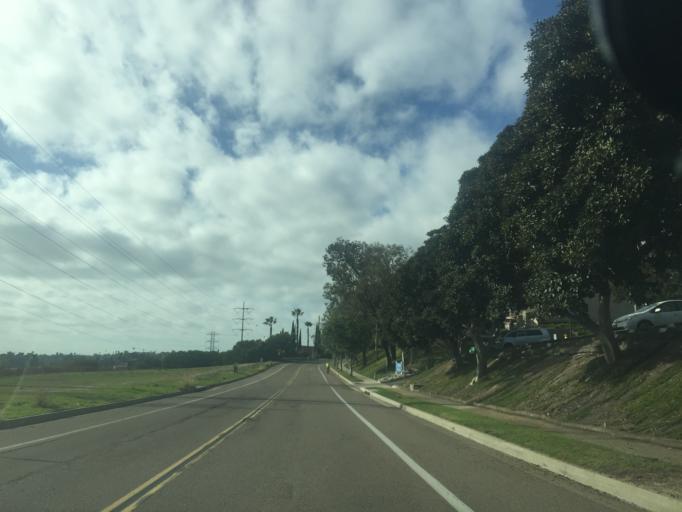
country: US
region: California
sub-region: San Diego County
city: San Diego
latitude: 32.7843
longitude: -117.1479
